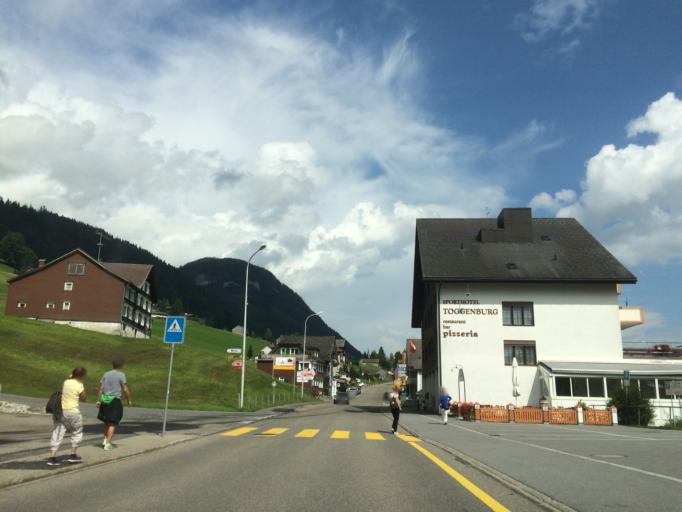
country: CH
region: Saint Gallen
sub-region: Wahlkreis Toggenburg
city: Wildhaus
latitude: 47.2011
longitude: 9.3385
